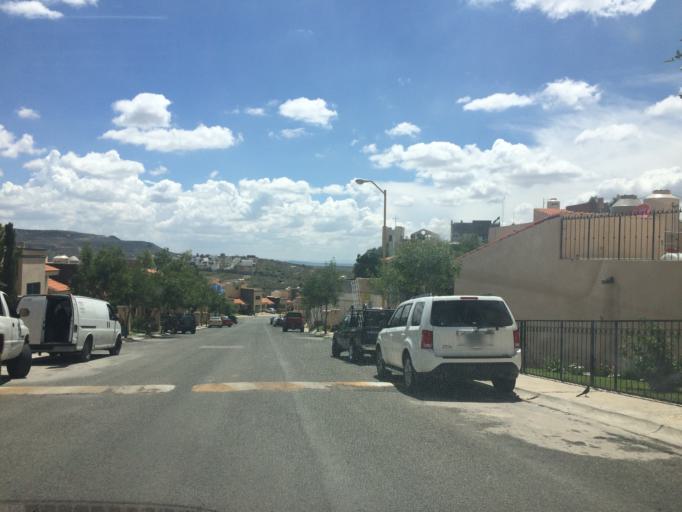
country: MX
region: Zacatecas
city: Zacatecas
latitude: 22.7482
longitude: -102.5925
